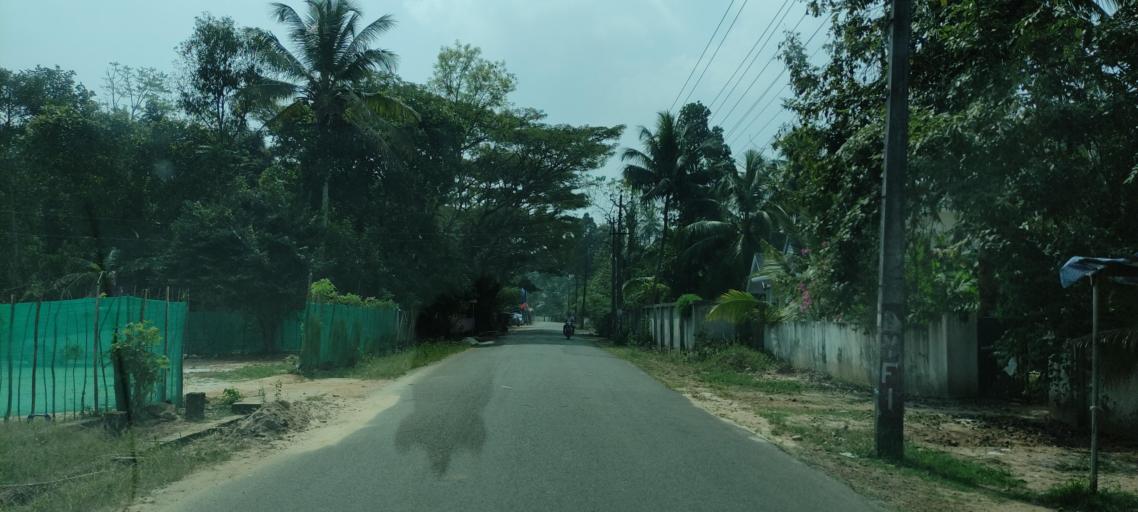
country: IN
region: Kerala
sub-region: Alappuzha
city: Shertallai
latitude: 9.6539
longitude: 76.3576
